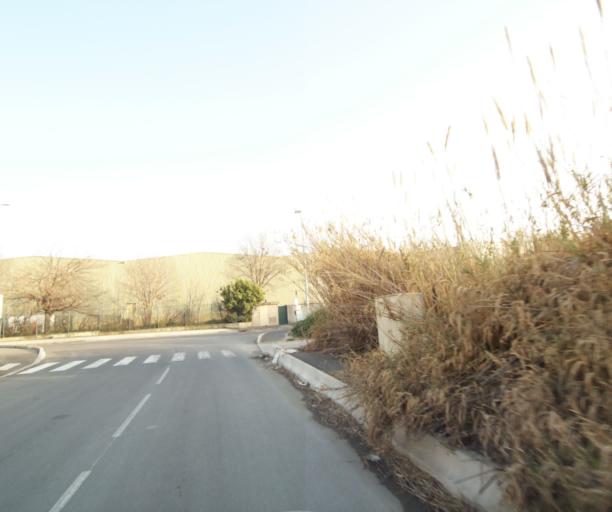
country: FR
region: Provence-Alpes-Cote d'Azur
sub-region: Departement des Bouches-du-Rhone
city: Saint-Victoret
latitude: 43.4187
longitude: 5.2641
